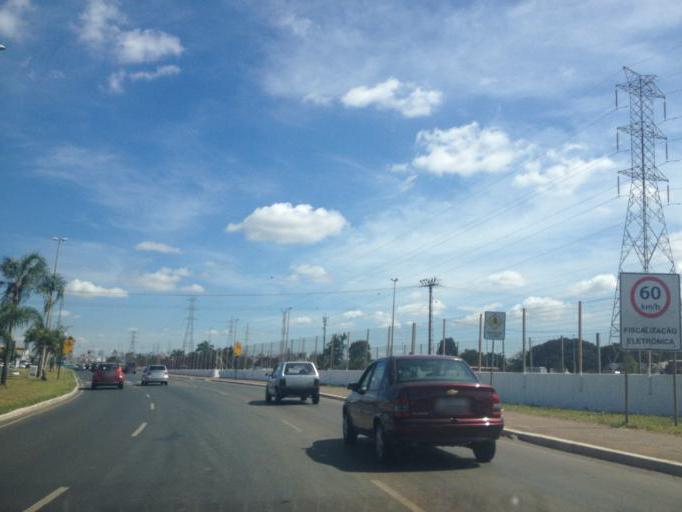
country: BR
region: Federal District
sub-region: Brasilia
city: Brasilia
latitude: -15.8245
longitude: -47.9781
